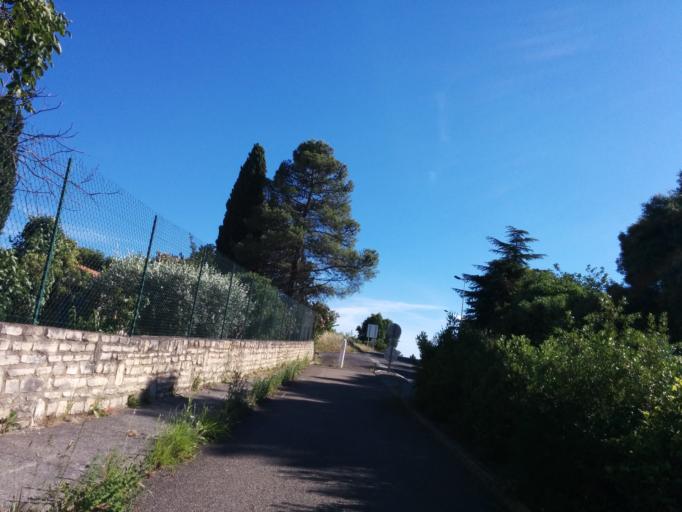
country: FR
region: Languedoc-Roussillon
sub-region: Departement du Gard
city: Saint-Christol-les-Ales
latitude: 44.0898
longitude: 4.0642
